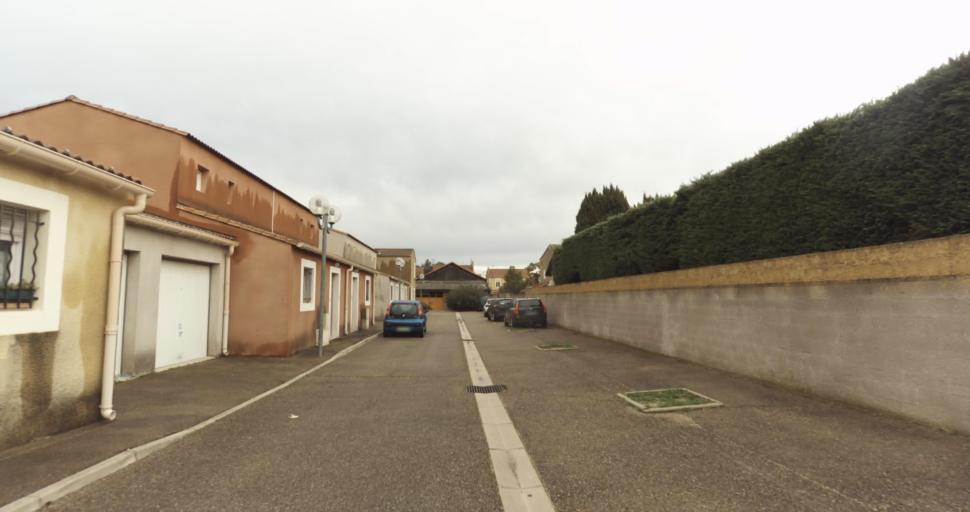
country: FR
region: Provence-Alpes-Cote d'Azur
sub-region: Departement des Bouches-du-Rhone
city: Rognonas
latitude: 43.8971
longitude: 4.7989
